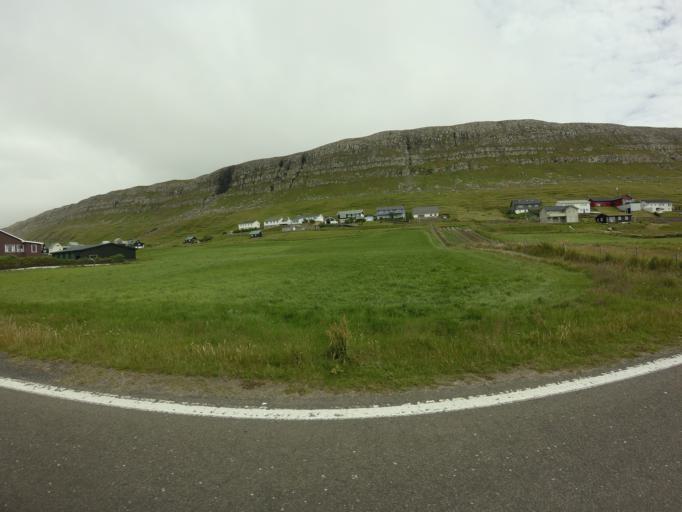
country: FO
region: Sandoy
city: Sandur
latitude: 61.8403
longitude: -6.8087
